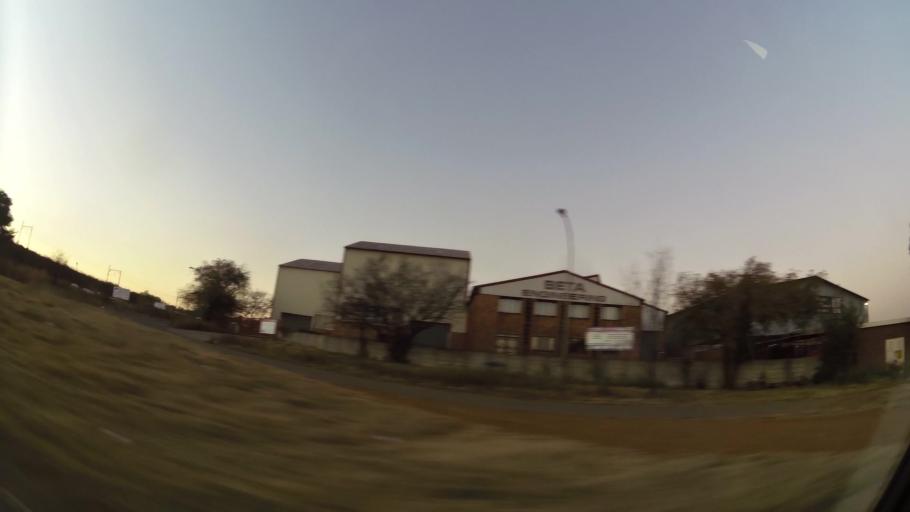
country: ZA
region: Gauteng
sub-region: Ekurhuleni Metropolitan Municipality
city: Germiston
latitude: -26.2625
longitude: 28.1692
